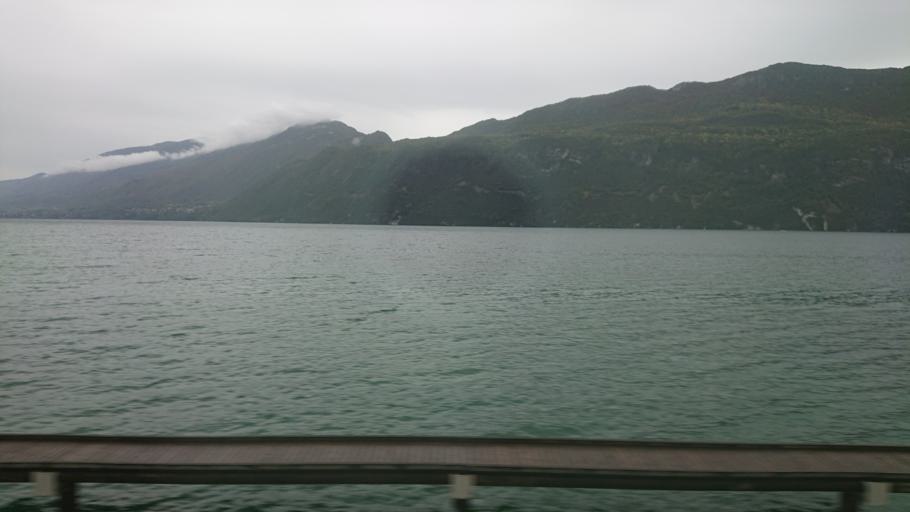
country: FR
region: Rhone-Alpes
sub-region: Departement de la Savoie
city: Brison-Saint-Innocent
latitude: 45.7177
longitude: 5.8852
